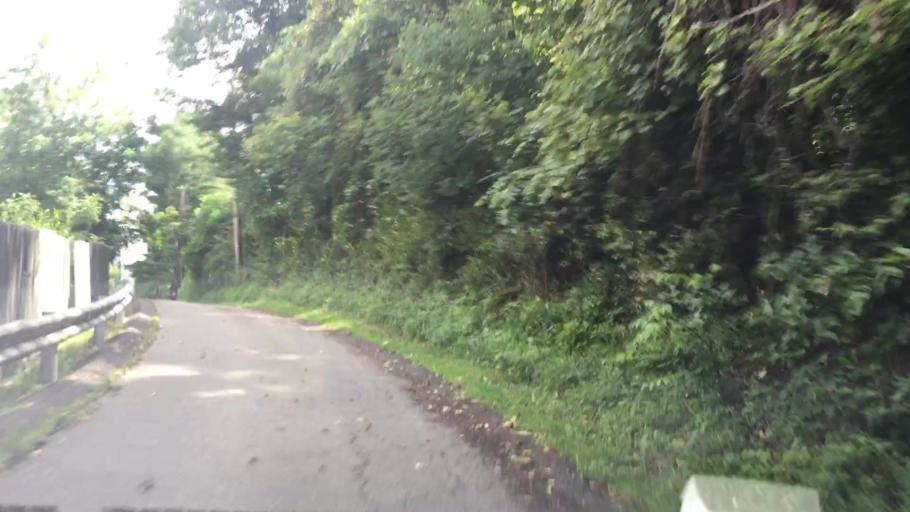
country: US
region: Pennsylvania
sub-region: Allegheny County
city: Russellton
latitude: 40.5704
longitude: -79.8658
